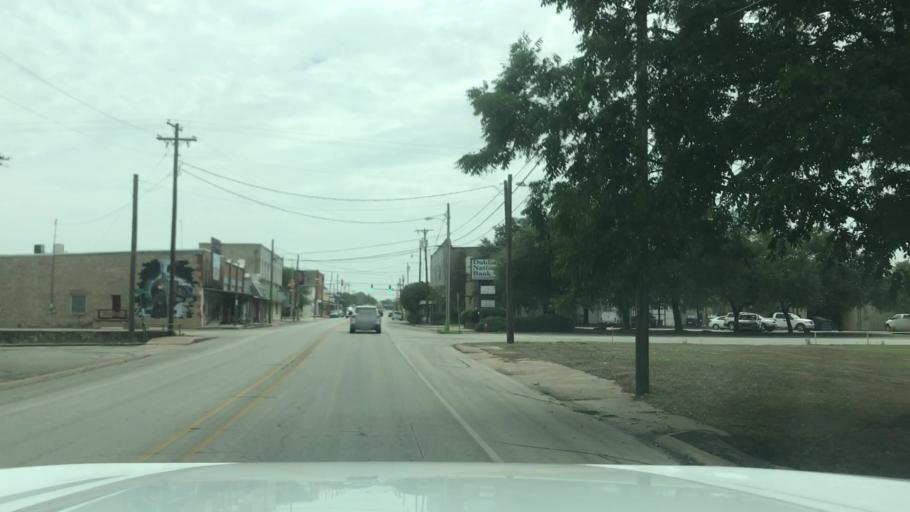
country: US
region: Texas
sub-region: Erath County
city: Dublin
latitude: 32.0855
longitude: -98.3440
